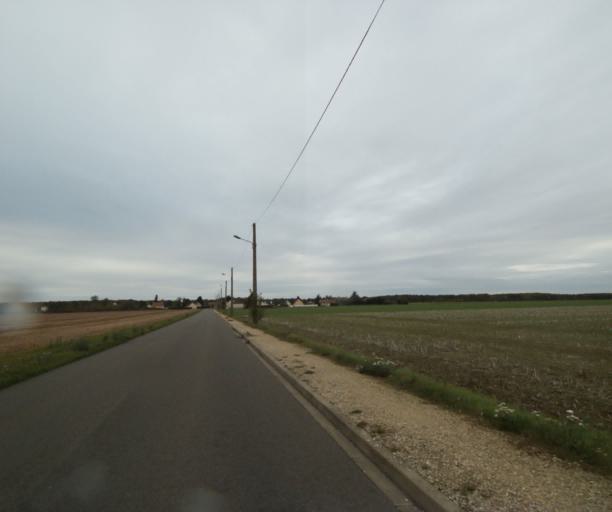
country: FR
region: Centre
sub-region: Departement d'Eure-et-Loir
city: Dreux
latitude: 48.7522
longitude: 1.3421
